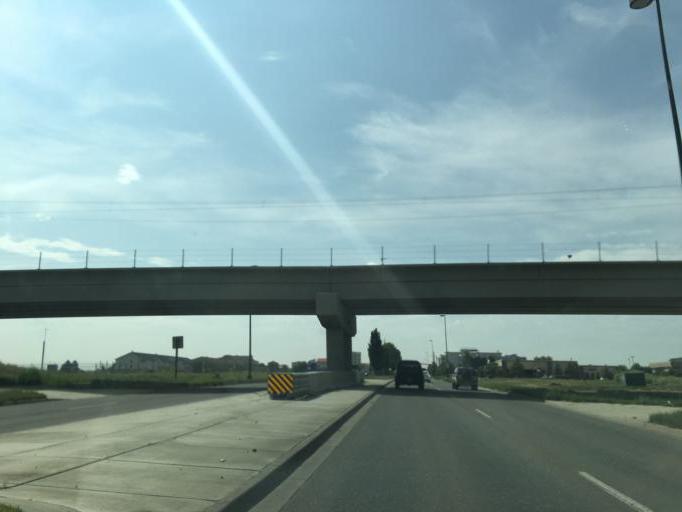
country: US
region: Colorado
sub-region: Adams County
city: Aurora
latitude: 39.8284
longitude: -104.7720
